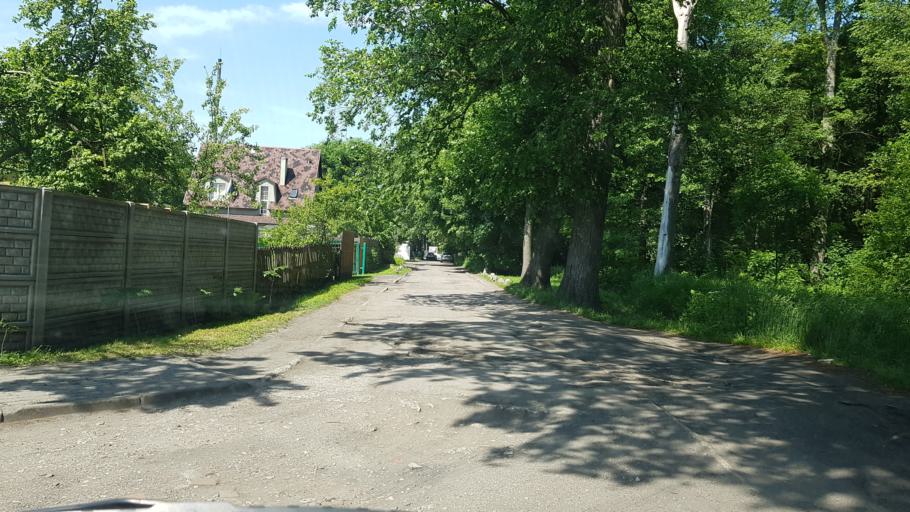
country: RU
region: Kaliningrad
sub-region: Gorod Kaliningrad
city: Baltiysk
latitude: 54.6483
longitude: 19.8902
